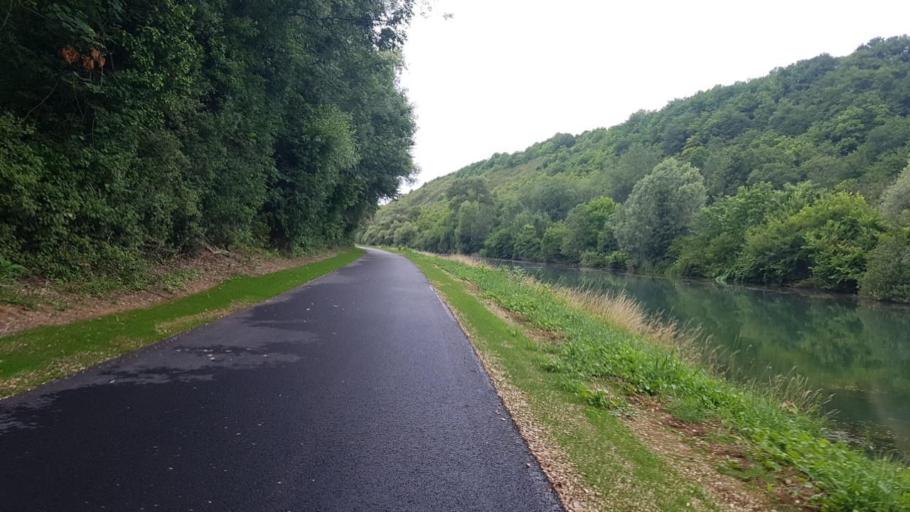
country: FR
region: Champagne-Ardenne
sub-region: Departement de la Marne
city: Vitry-le-Francois
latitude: 48.7684
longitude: 4.5573
